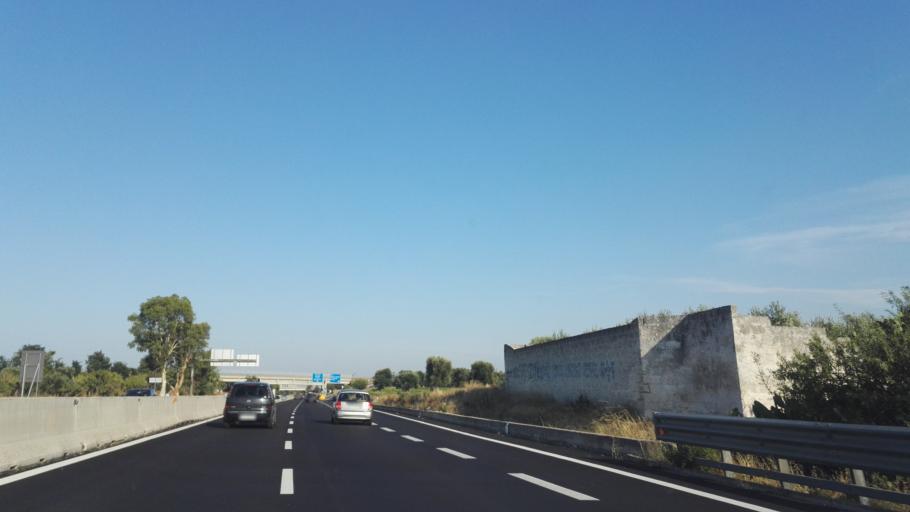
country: IT
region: Apulia
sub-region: Provincia di Brindisi
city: Fasano
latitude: 40.8372
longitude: 17.3836
